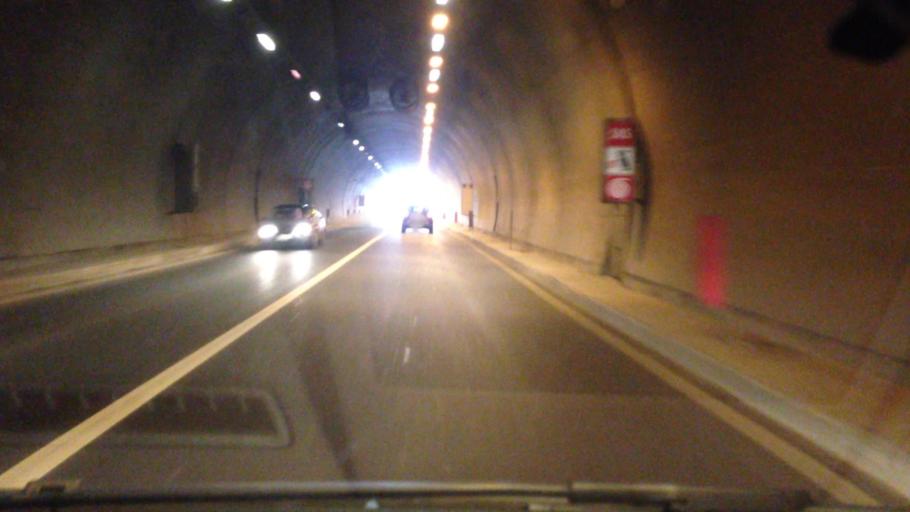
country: IT
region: Piedmont
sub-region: Provincia di Asti
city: Piano-Molini d'Isola
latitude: 44.8385
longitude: 8.1968
